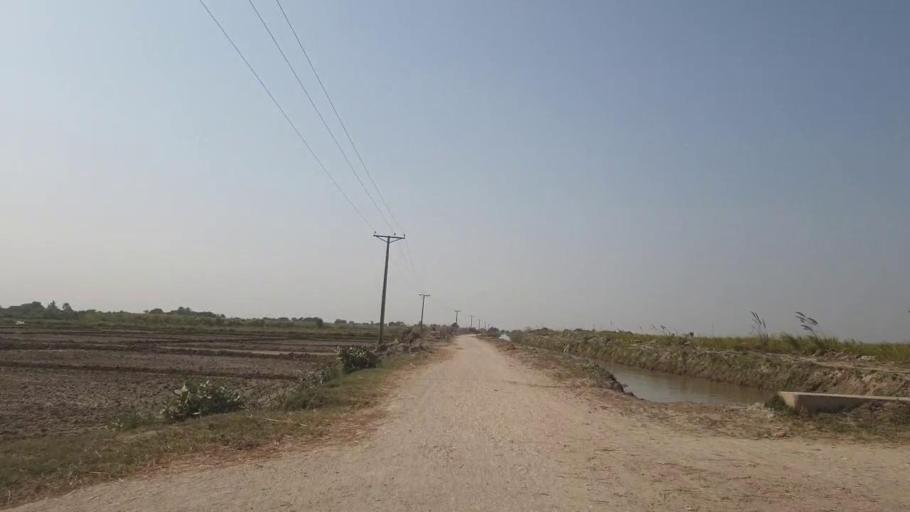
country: PK
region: Sindh
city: Bulri
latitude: 24.9520
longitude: 68.3778
